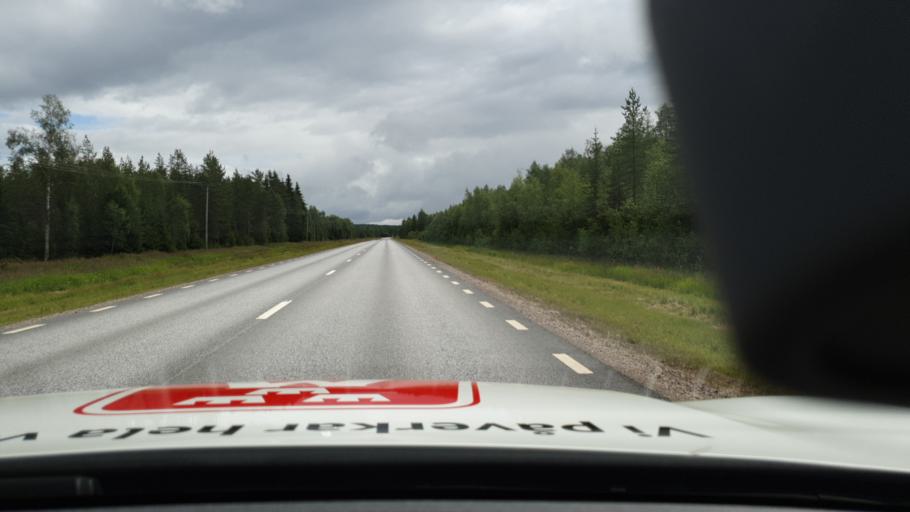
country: SE
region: Norrbotten
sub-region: Pitea Kommun
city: Rosvik
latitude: 65.5773
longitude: 21.7154
